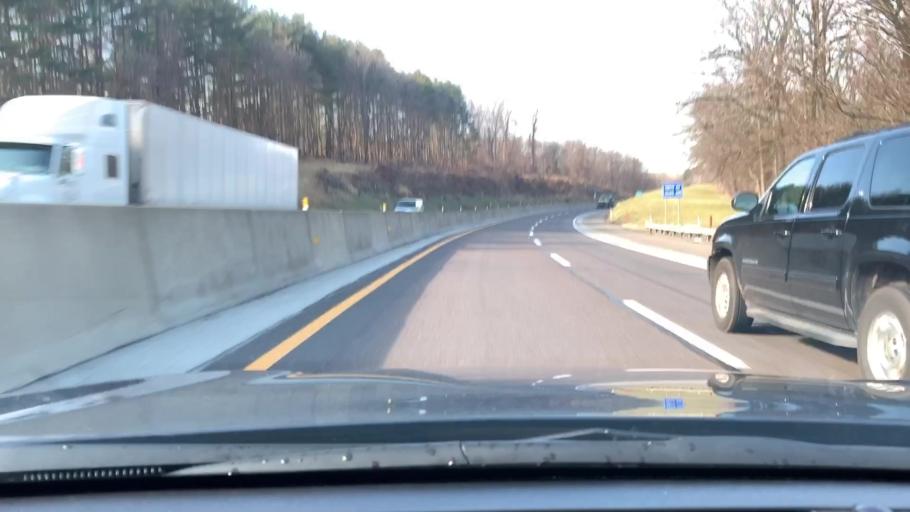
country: US
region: Pennsylvania
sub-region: Chester County
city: Exton
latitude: 40.0616
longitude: -75.6282
